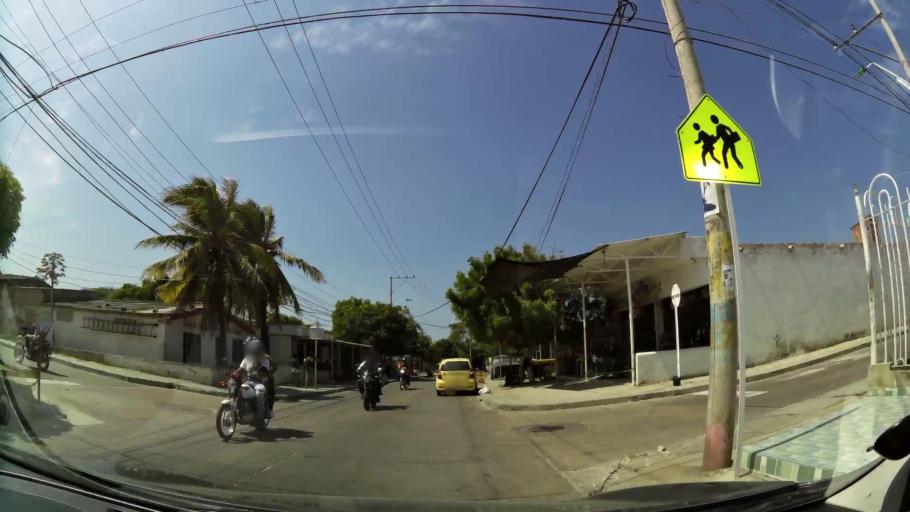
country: CO
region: Atlantico
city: Barranquilla
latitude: 10.9644
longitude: -74.8214
